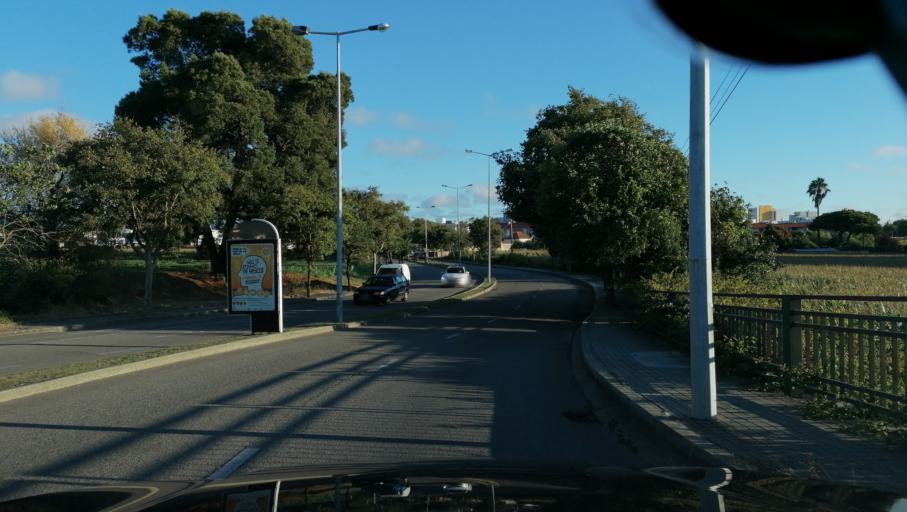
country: PT
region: Aveiro
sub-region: Aveiro
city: Aveiro
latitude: 40.6340
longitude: -8.6436
